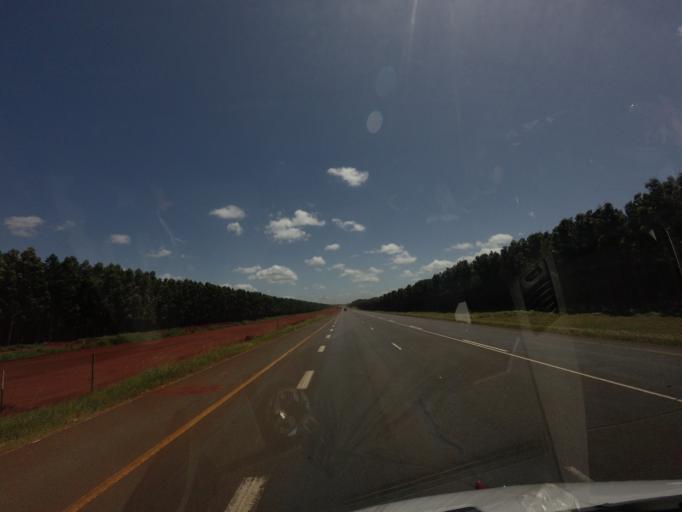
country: ZA
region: KwaZulu-Natal
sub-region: uThungulu District Municipality
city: Empangeni
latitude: -28.7608
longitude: 31.9332
